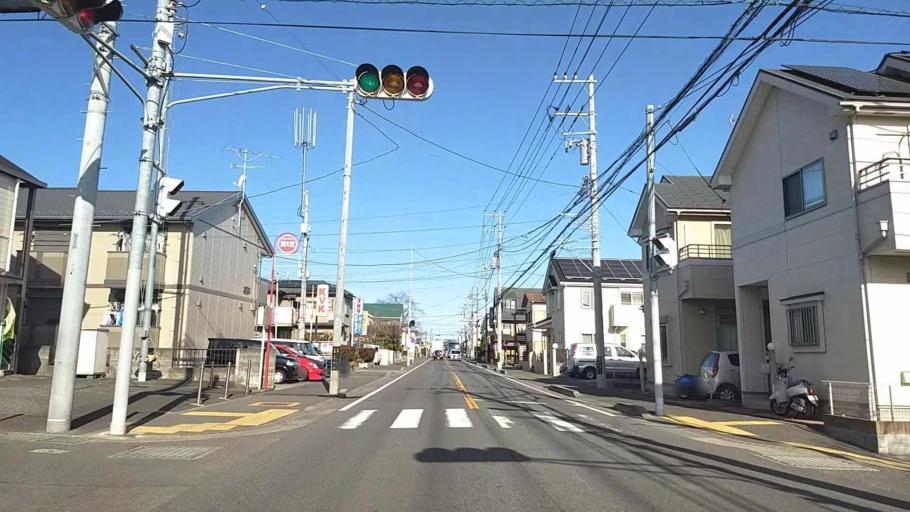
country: JP
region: Kanagawa
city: Atsugi
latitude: 35.4581
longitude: 139.3478
